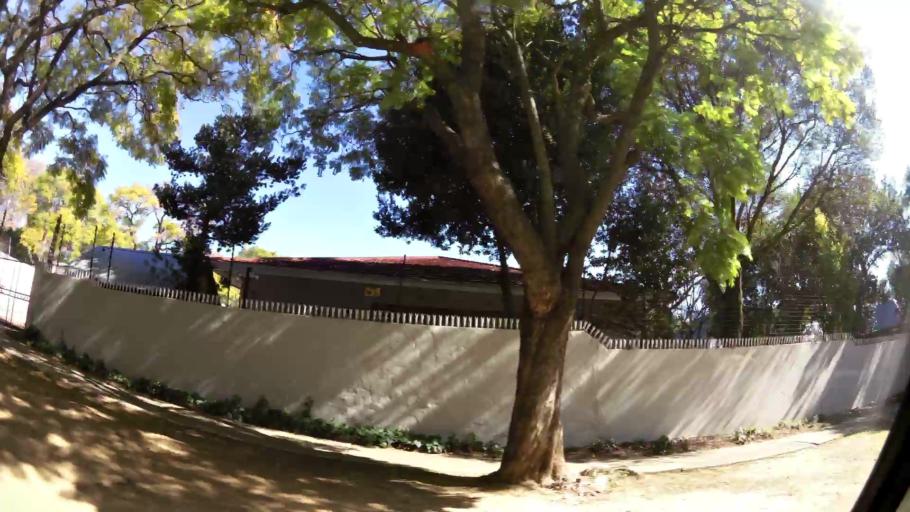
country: ZA
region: Gauteng
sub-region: City of Tshwane Metropolitan Municipality
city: Pretoria
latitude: -25.7740
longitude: 28.2484
